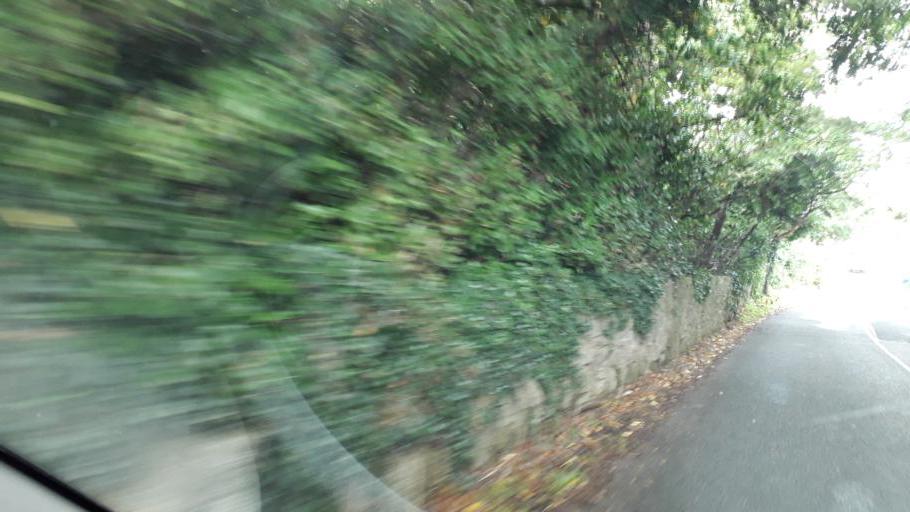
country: IE
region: Leinster
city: Sandyford
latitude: 53.2561
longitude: -6.2206
